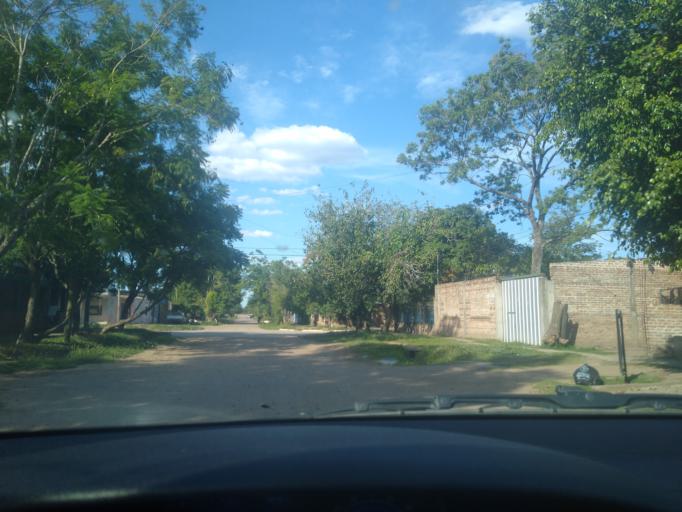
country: AR
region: Chaco
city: Barranqueras
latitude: -27.4707
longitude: -58.9347
